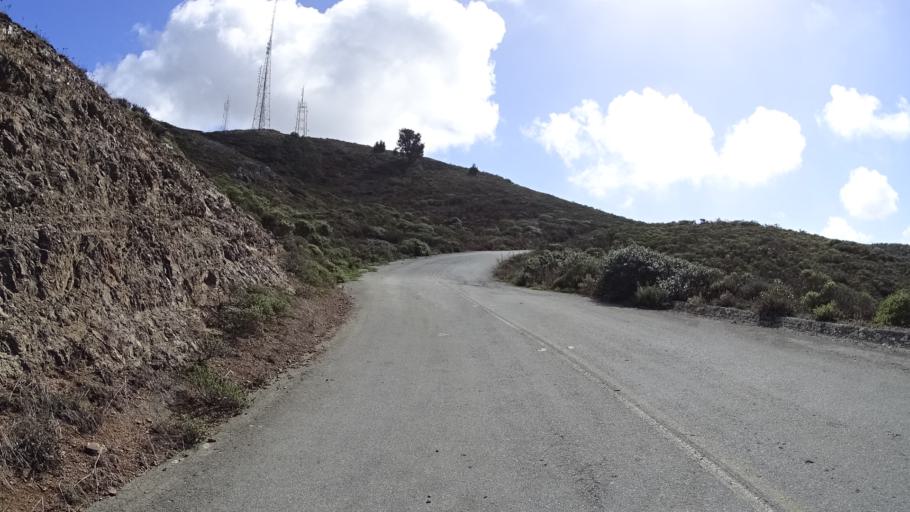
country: US
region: California
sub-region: San Mateo County
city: Colma
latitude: 37.6915
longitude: -122.4404
